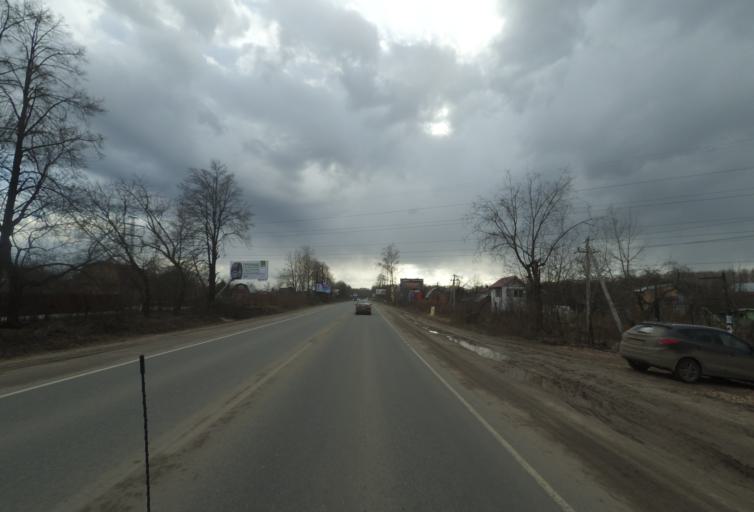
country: RU
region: Nizjnij Novgorod
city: Afonino
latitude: 56.2243
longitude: 44.0903
